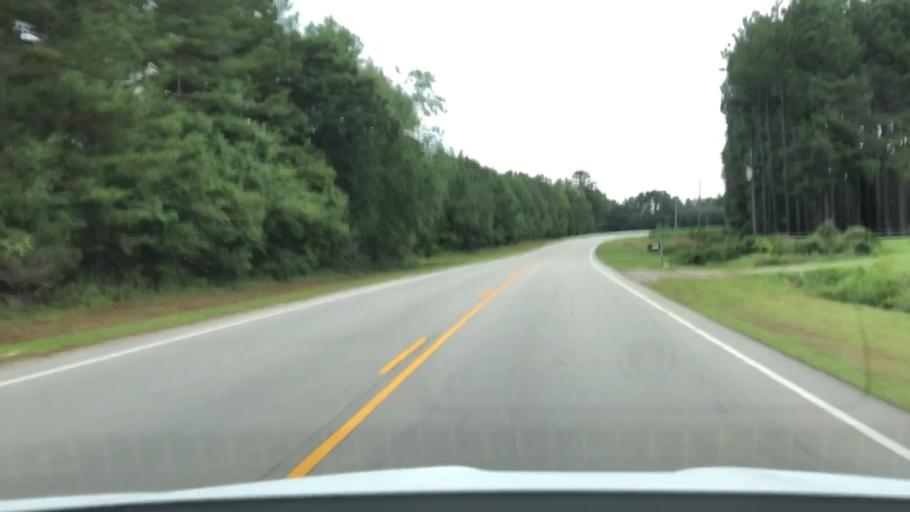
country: US
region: North Carolina
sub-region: Jones County
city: Trenton
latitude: 35.0388
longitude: -77.3475
